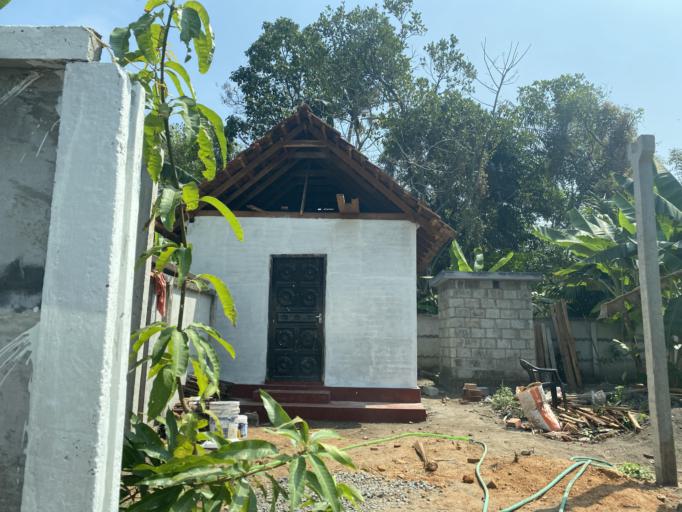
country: IN
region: Kerala
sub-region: Ernakulam
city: Elur
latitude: 10.1078
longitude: 76.2302
